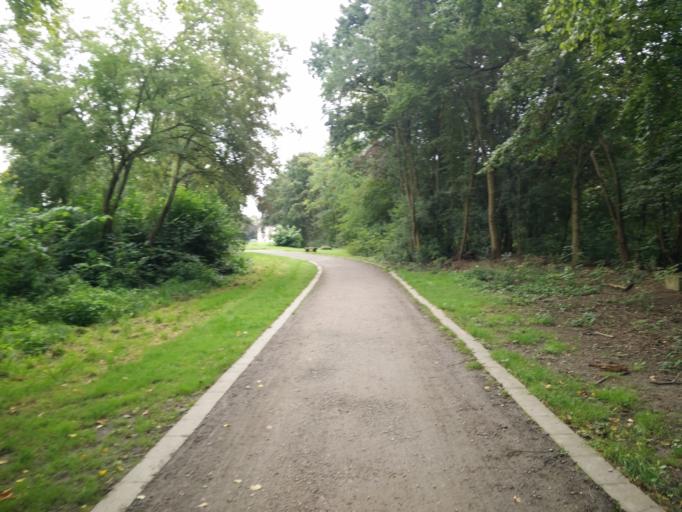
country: DE
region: North Rhine-Westphalia
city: Bochum-Hordel
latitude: 51.5011
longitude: 7.1853
